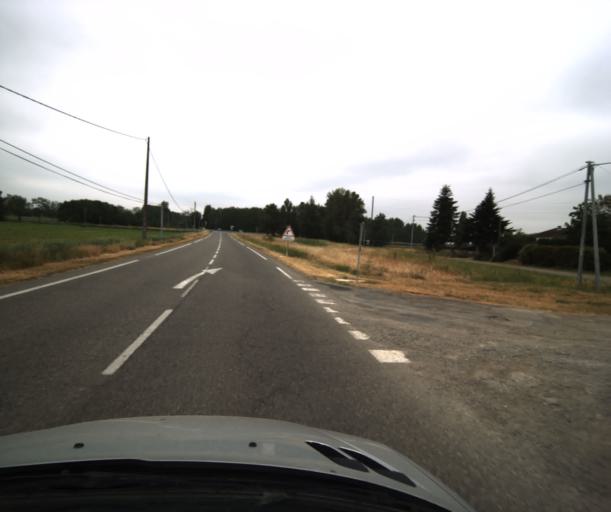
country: FR
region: Midi-Pyrenees
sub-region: Departement du Tarn-et-Garonne
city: Saint-Nicolas-de-la-Grave
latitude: 44.0754
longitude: 0.9978
